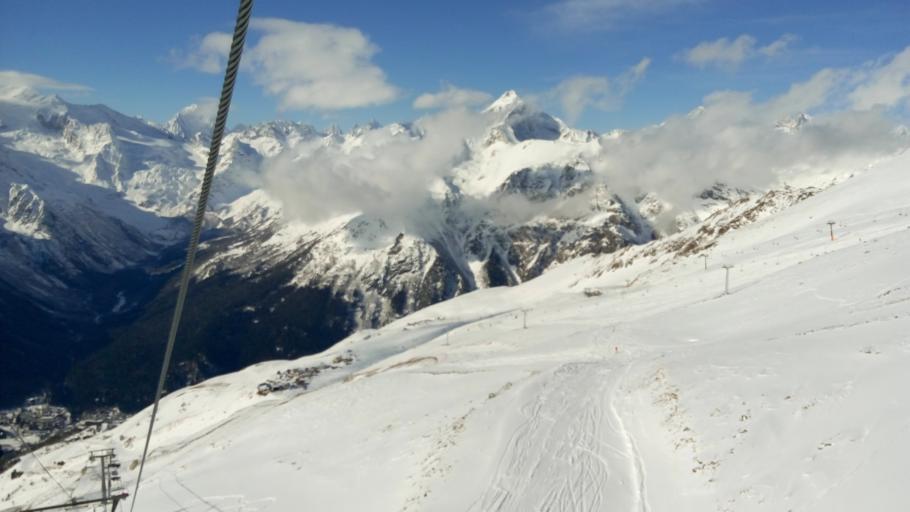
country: RU
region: Karachayevo-Cherkesiya
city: Teberda
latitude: 43.2912
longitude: 41.6704
